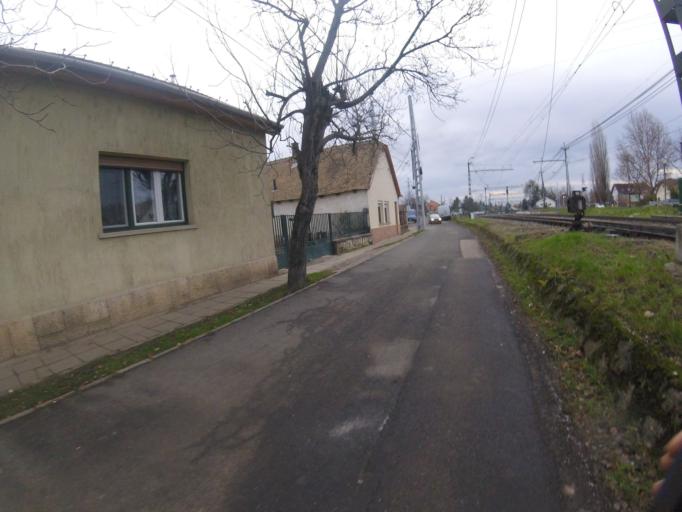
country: HU
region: Pest
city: Budakalasz
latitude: 47.6175
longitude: 19.0535
